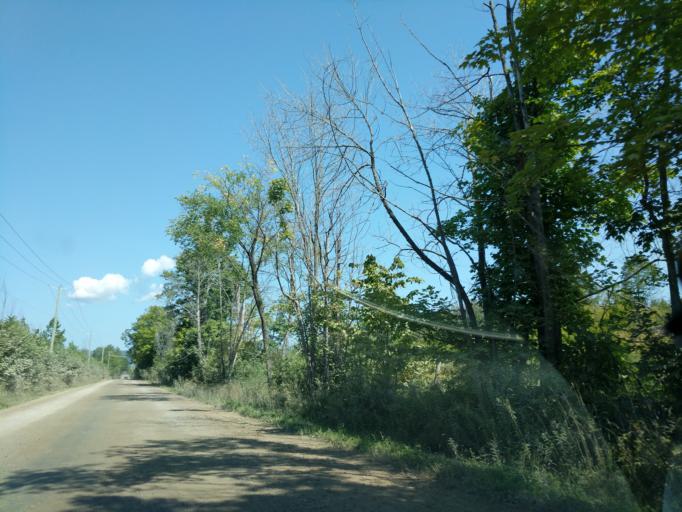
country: CA
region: Ontario
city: Bells Corners
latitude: 45.4440
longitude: -75.9026
